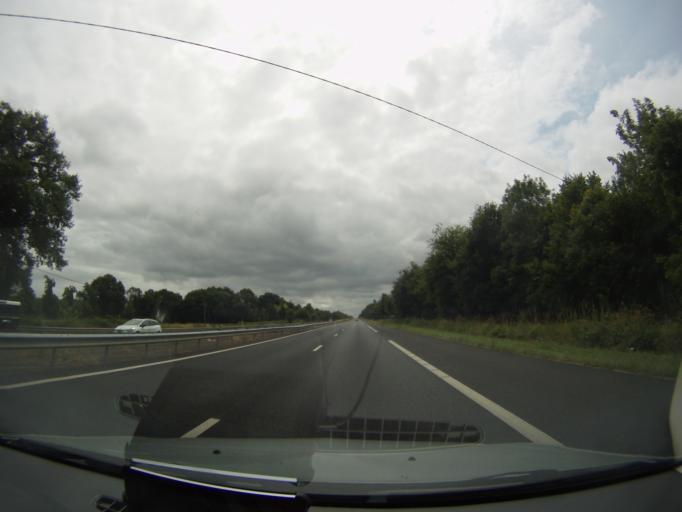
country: FR
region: Pays de la Loire
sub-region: Departement de la Loire-Atlantique
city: Derval
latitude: 47.6422
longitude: -1.6555
